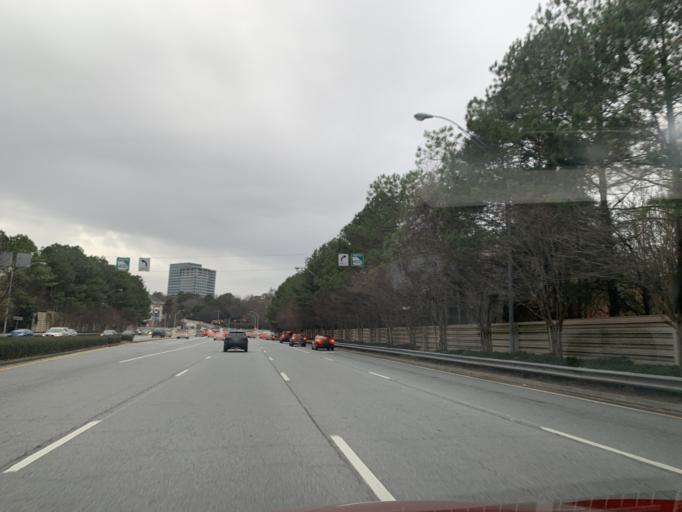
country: US
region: Georgia
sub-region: DeKalb County
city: North Atlanta
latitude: 33.8527
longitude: -84.3671
